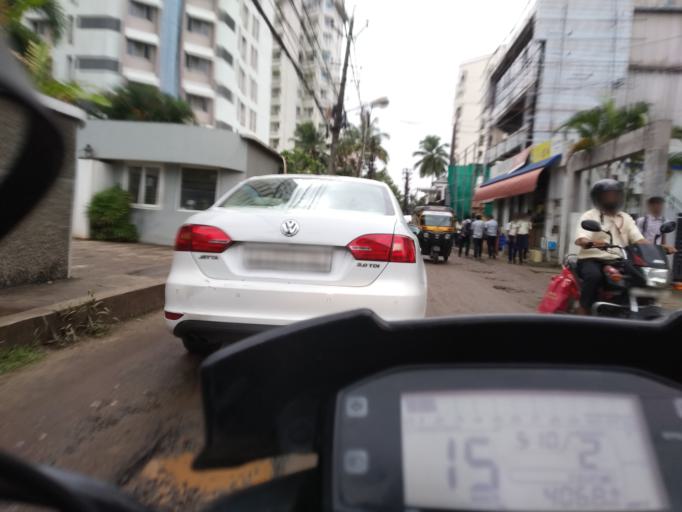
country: IN
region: Kerala
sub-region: Ernakulam
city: Cochin
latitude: 9.9341
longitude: 76.2983
